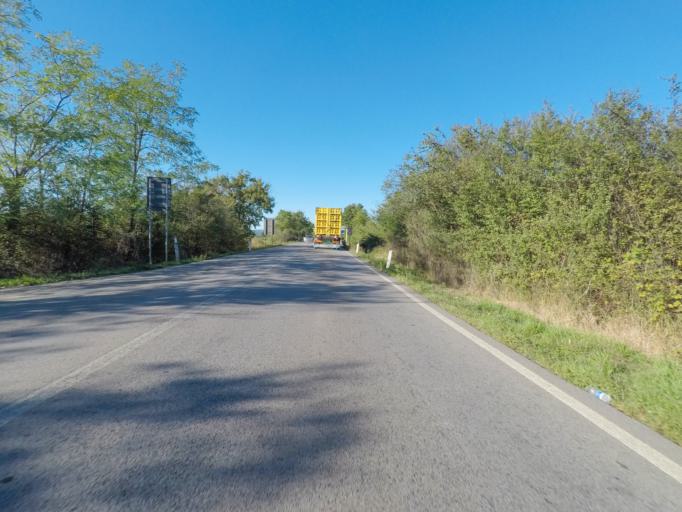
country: IT
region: Tuscany
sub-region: Provincia di Siena
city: Rosia
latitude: 43.2175
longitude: 11.2757
